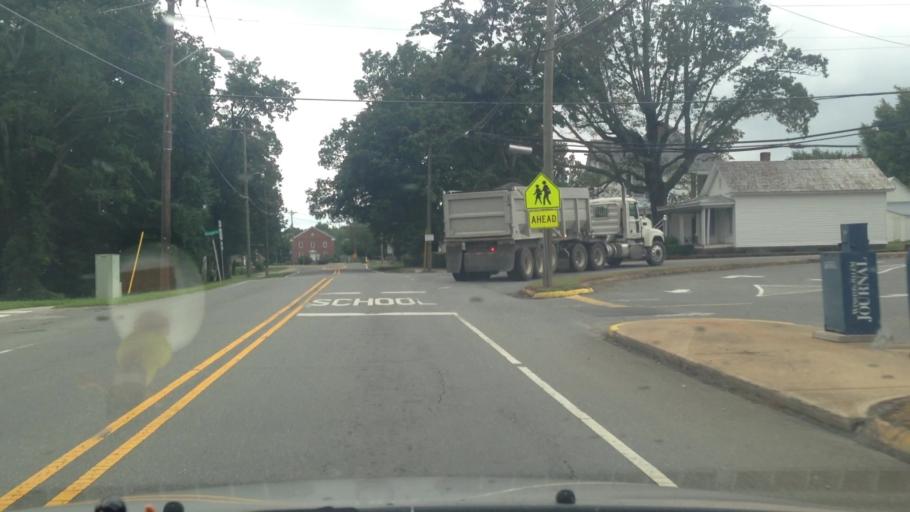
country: US
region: North Carolina
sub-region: Forsyth County
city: Walkertown
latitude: 36.1746
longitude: -80.1530
